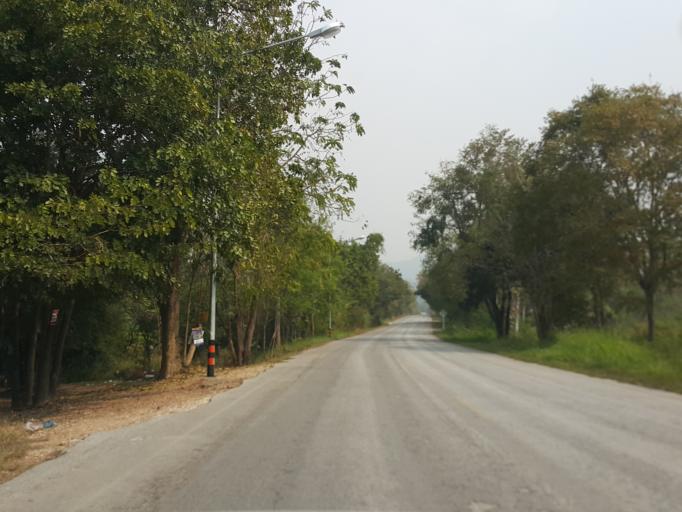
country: TH
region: Lampang
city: Thoen
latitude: 17.6307
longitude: 99.2585
